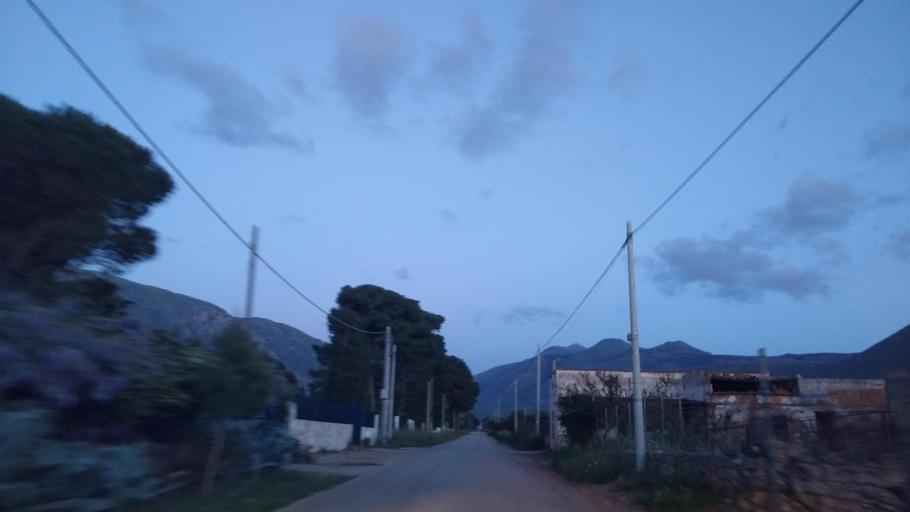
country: IT
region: Sicily
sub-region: Trapani
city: Castelluzzo
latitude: 38.1094
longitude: 12.7259
